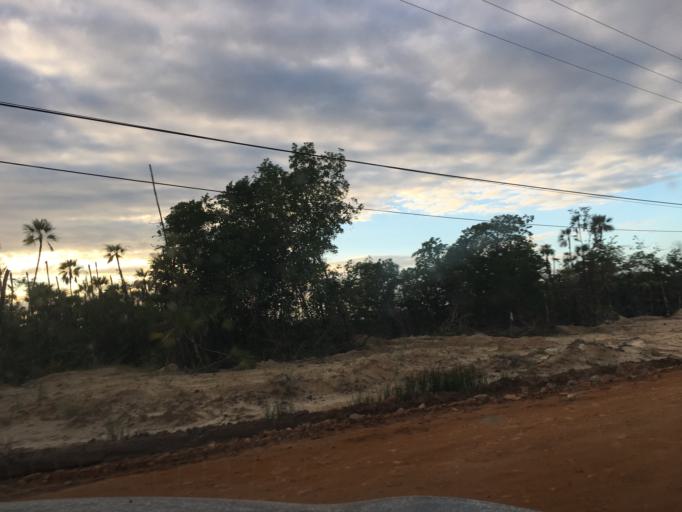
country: BZ
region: Stann Creek
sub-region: Dangriga
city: Dangriga
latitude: 16.8340
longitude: -88.2656
